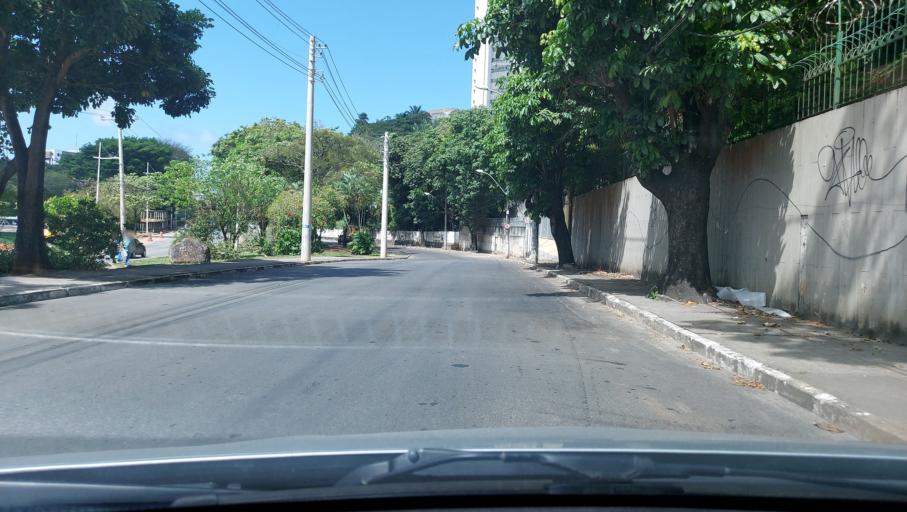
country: BR
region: Bahia
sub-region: Salvador
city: Salvador
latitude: -12.9966
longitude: -38.4785
